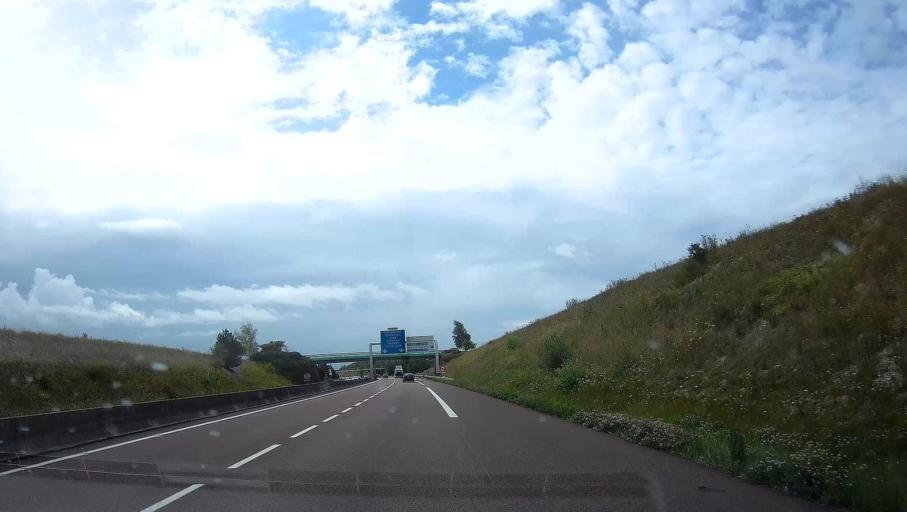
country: FR
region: Champagne-Ardenne
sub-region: Departement de l'Aube
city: Creney-pres-Troyes
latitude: 48.4181
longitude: 4.1457
